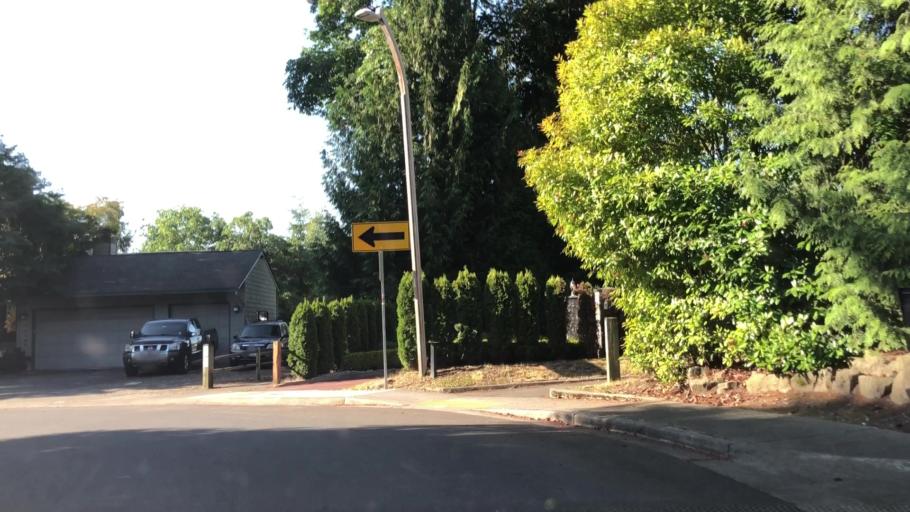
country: US
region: Washington
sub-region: King County
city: Eastgate
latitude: 47.6199
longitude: -122.1487
